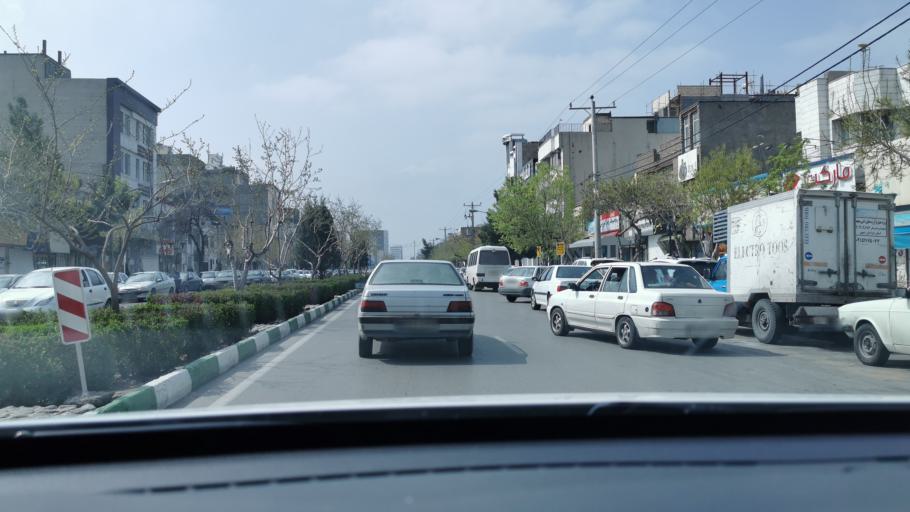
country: IR
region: Razavi Khorasan
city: Mashhad
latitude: 36.3269
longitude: 59.5400
